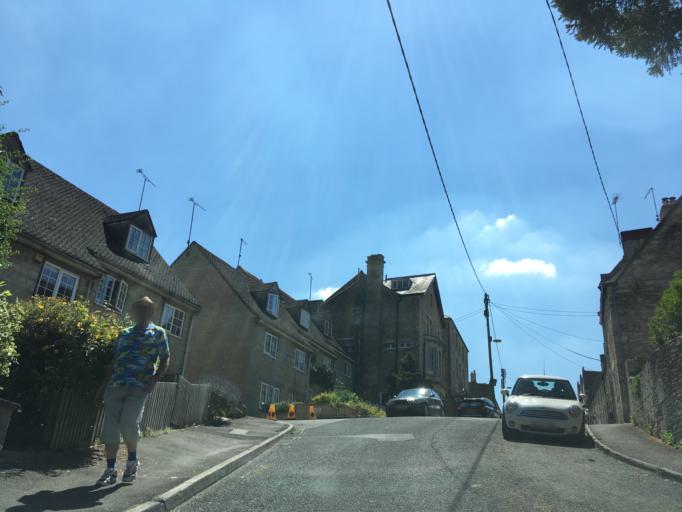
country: GB
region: England
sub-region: Gloucestershire
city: Tetbury
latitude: 51.6378
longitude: -2.1570
